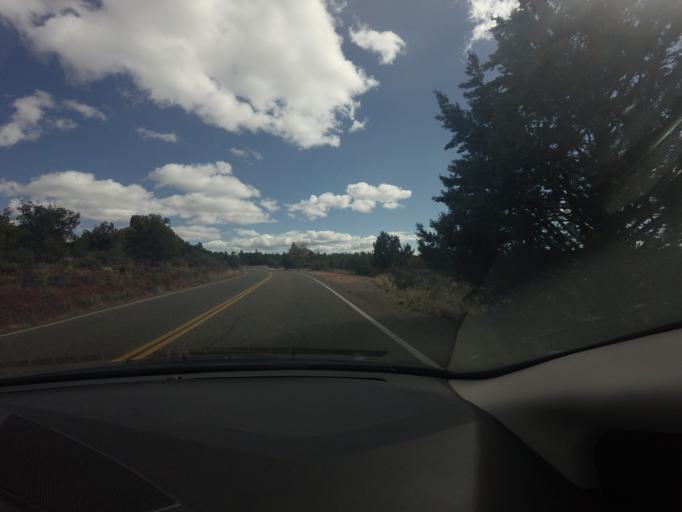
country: US
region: Arizona
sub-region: Yavapai County
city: West Sedona
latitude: 34.8827
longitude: -111.8213
